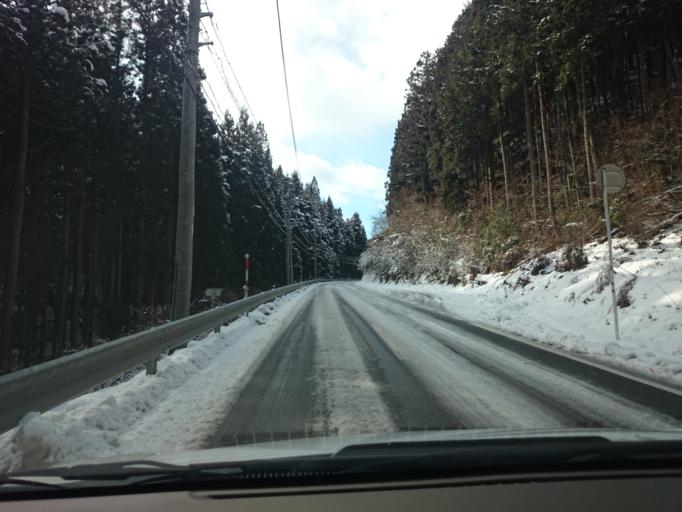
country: JP
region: Gifu
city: Gujo
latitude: 35.7448
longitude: 137.0257
